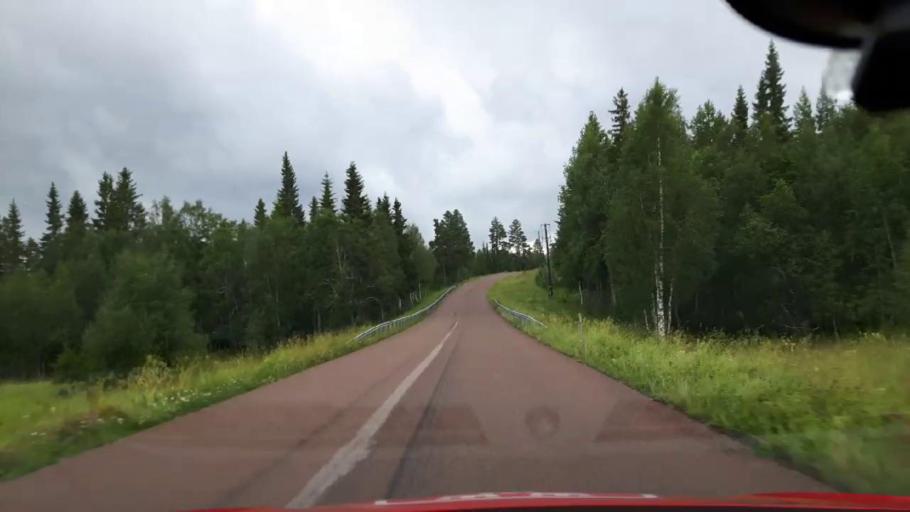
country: SE
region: Jaemtland
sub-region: Krokoms Kommun
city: Valla
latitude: 63.3466
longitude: 13.7224
